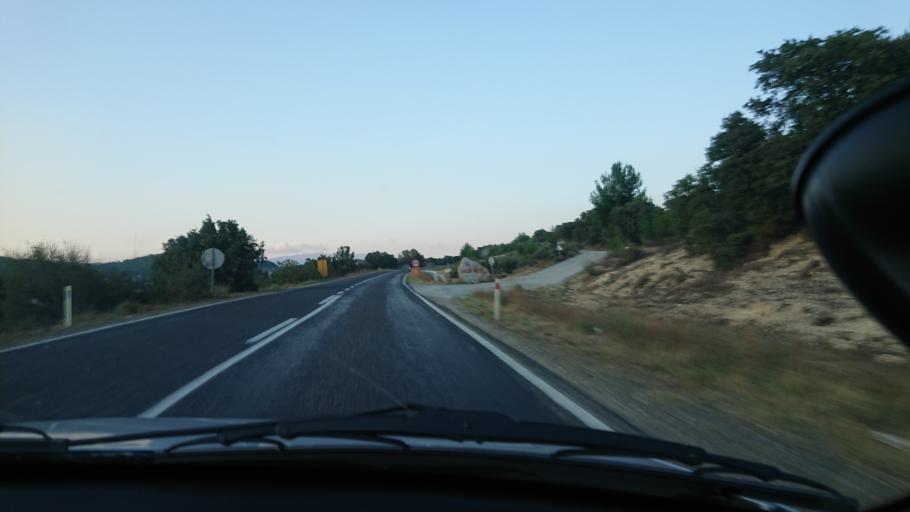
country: TR
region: Usak
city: Gure
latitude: 38.8044
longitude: 29.2371
